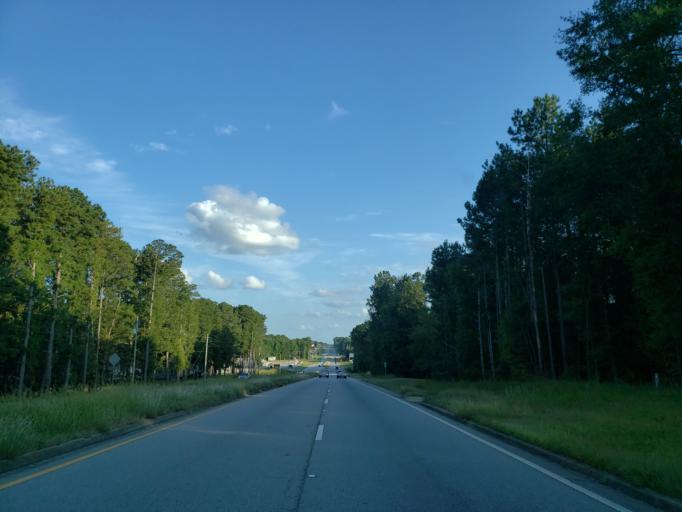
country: US
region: Georgia
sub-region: Carroll County
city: Mount Zion
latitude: 33.6584
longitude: -85.1442
